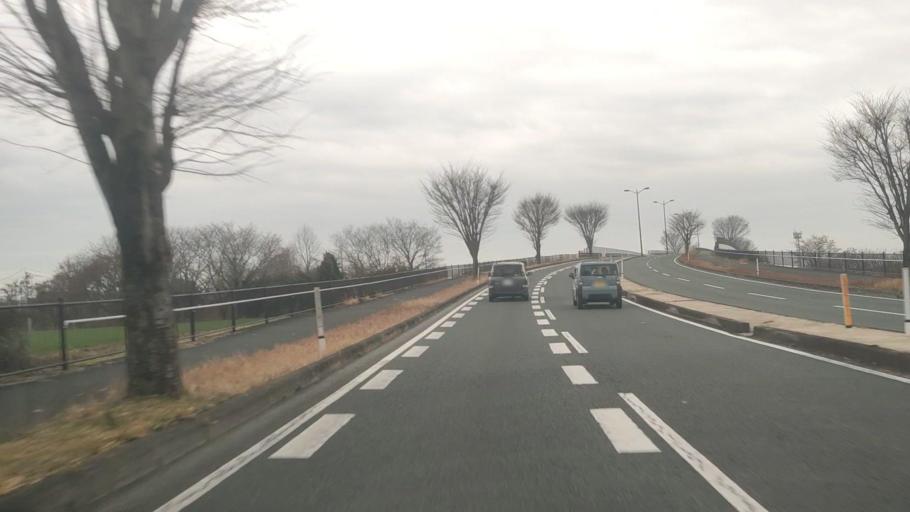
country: JP
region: Kumamoto
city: Ozu
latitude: 32.8204
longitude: 130.7907
